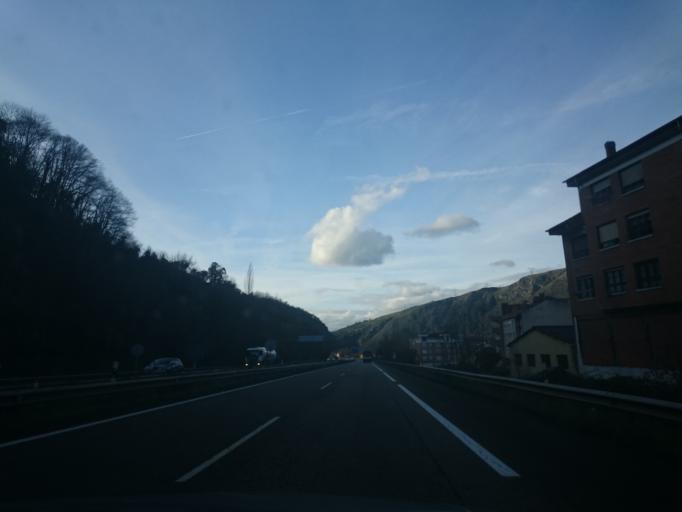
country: ES
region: Asturias
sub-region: Province of Asturias
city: Oviedo
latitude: 43.2971
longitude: -5.8204
